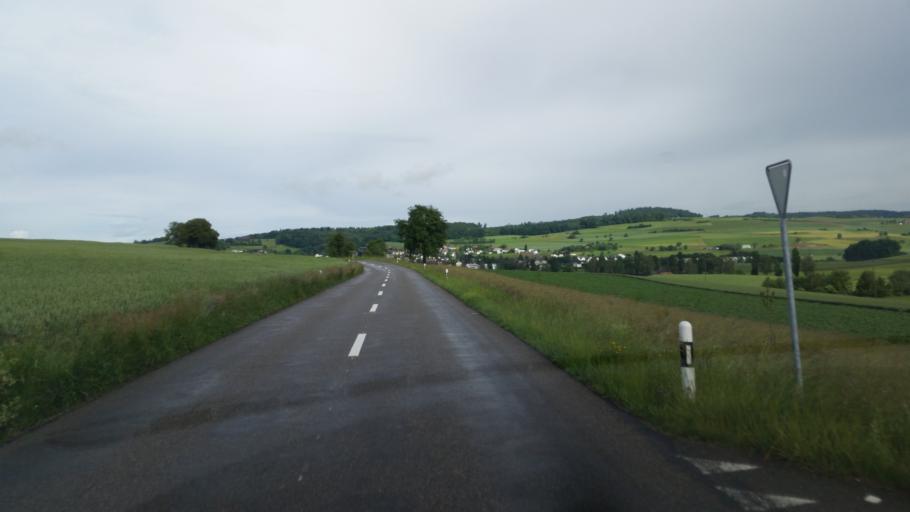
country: CH
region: Aargau
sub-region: Bezirk Lenzburg
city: Meisterschwanden
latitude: 47.3128
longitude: 8.2290
